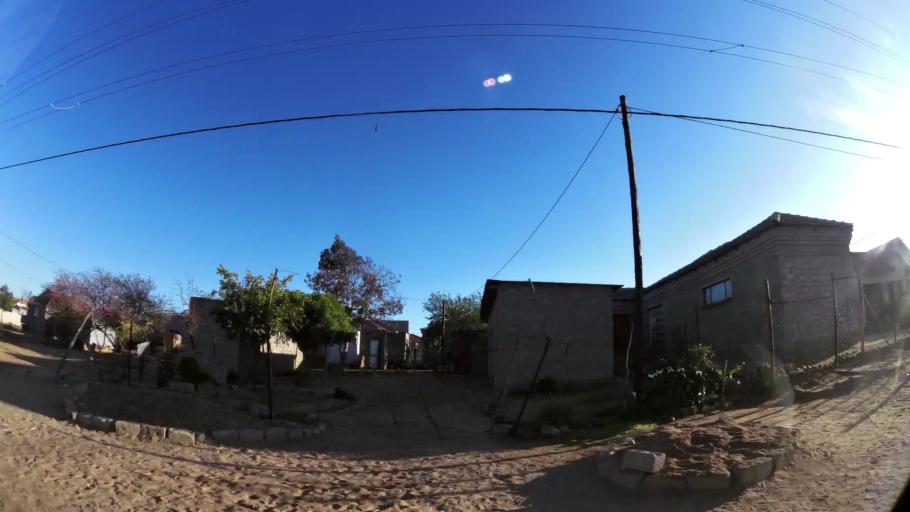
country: ZA
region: Limpopo
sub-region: Capricorn District Municipality
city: Polokwane
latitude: -23.8384
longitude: 29.3577
